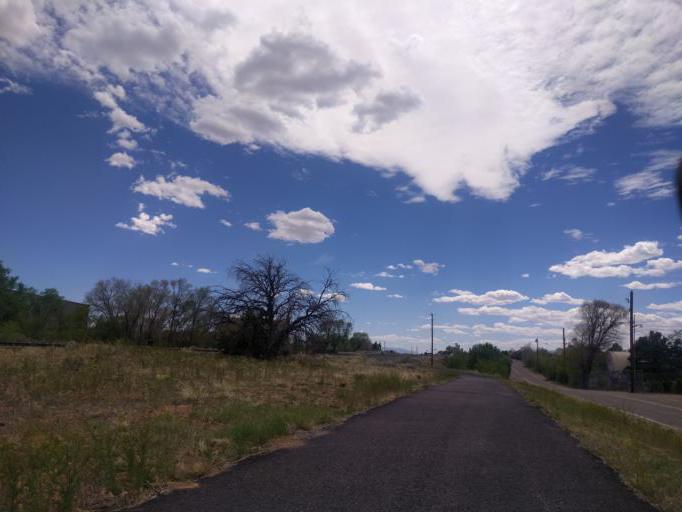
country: US
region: New Mexico
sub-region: Santa Fe County
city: Santa Fe
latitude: 35.6418
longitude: -105.9605
